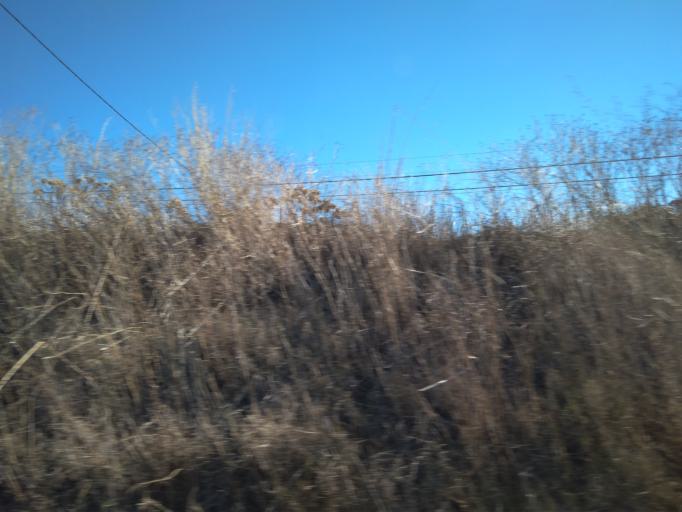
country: PT
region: Faro
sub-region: Faro
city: Faro
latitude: 37.0562
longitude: -7.9546
